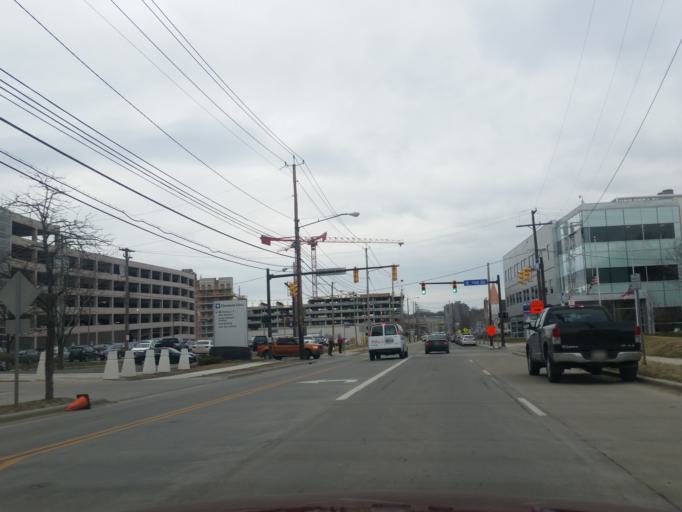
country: US
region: Ohio
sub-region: Cuyahoga County
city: Bratenahl
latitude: 41.4994
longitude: -81.6191
